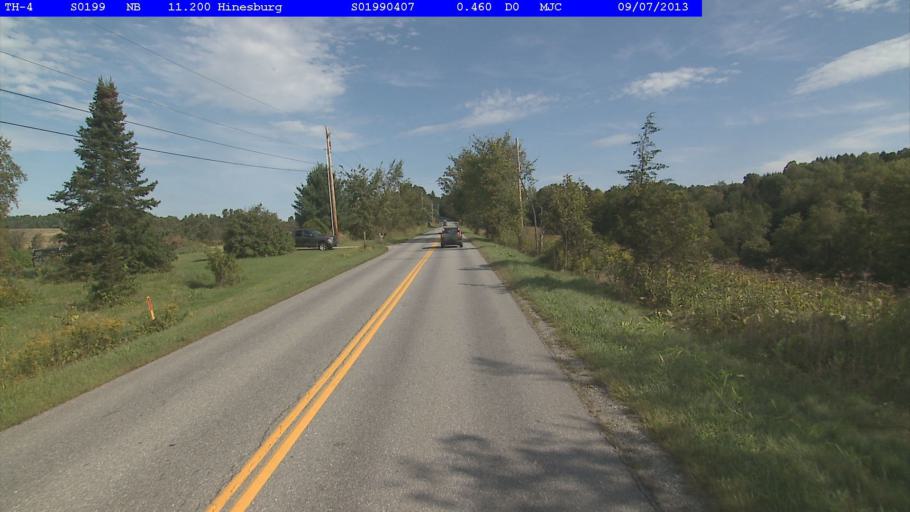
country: US
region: Vermont
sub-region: Chittenden County
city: Hinesburg
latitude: 44.2847
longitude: -73.1079
